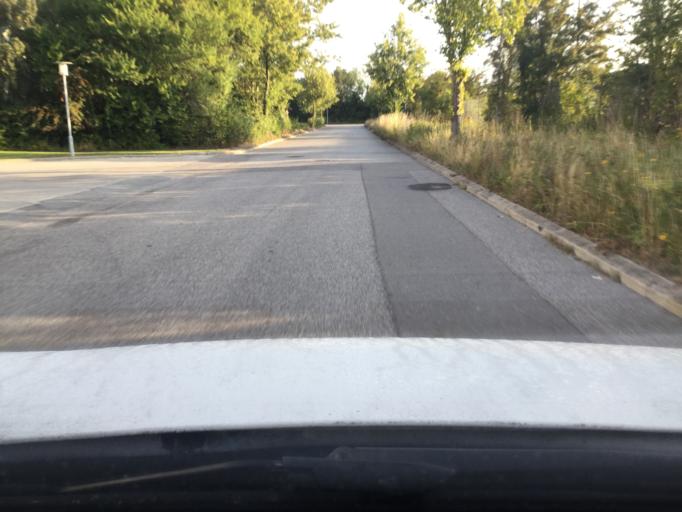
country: DK
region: Zealand
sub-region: Lolland Kommune
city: Nakskov
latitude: 54.8285
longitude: 11.1694
